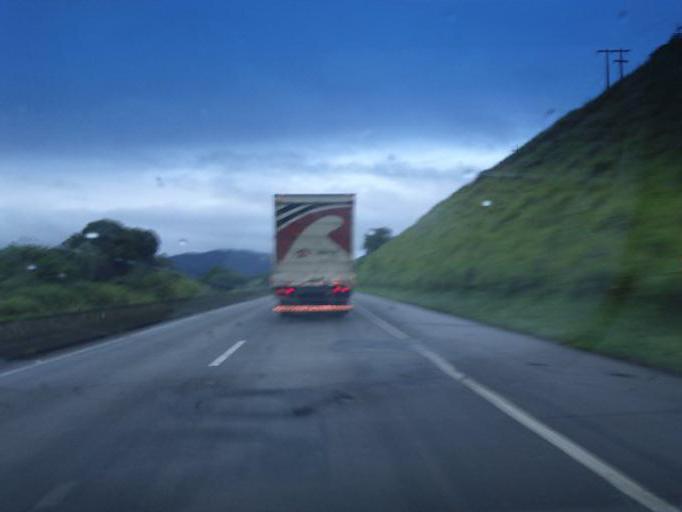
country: BR
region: Sao Paulo
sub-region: Miracatu
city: Miracatu
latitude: -24.1752
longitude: -47.3450
